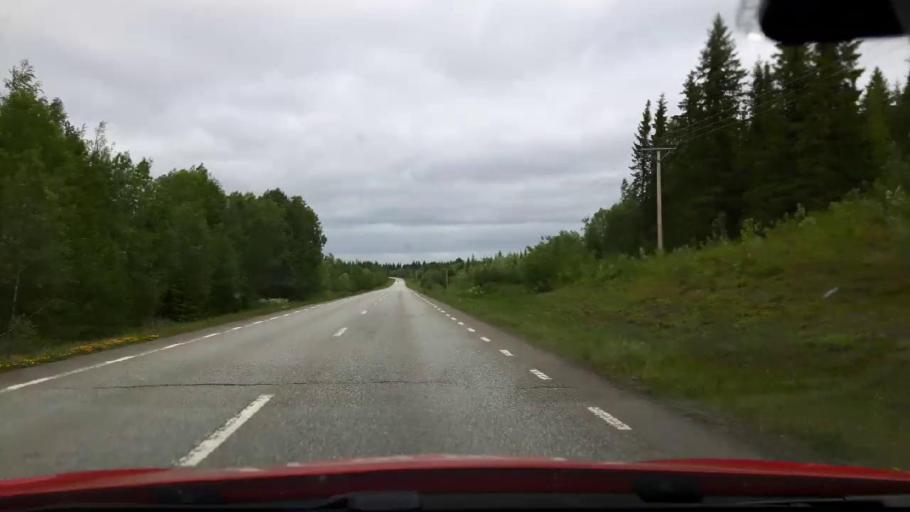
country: SE
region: Jaemtland
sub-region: Krokoms Kommun
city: Krokom
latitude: 63.5656
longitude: 14.6148
